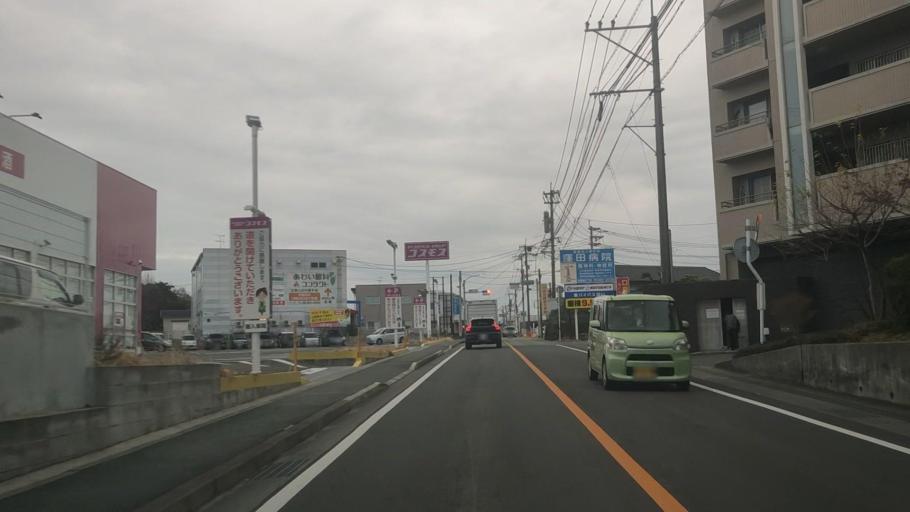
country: JP
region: Kumamoto
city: Kumamoto
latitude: 32.8139
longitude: 130.7542
